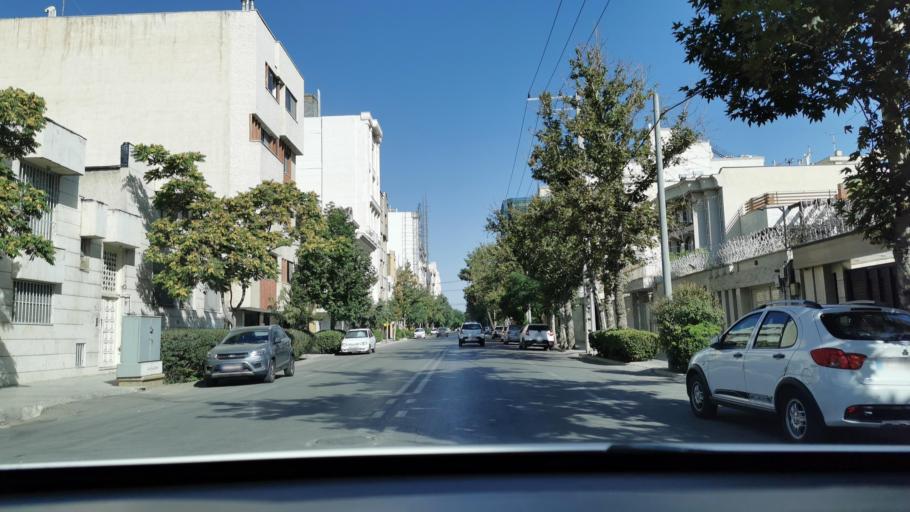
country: IR
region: Razavi Khorasan
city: Mashhad
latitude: 36.3138
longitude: 59.5495
